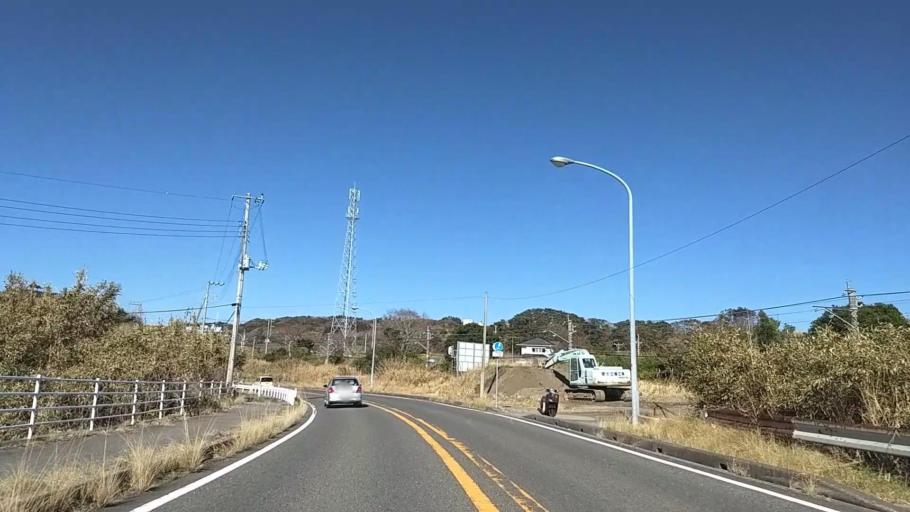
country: JP
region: Chiba
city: Kawaguchi
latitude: 35.0847
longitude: 140.0950
